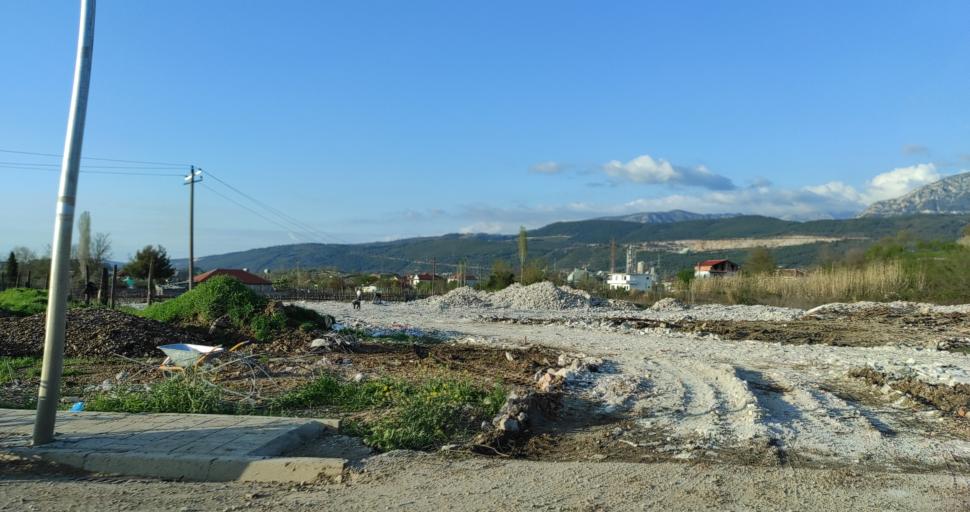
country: AL
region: Durres
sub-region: Rrethi i Krujes
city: Fushe-Kruje
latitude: 41.4852
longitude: 19.7304
